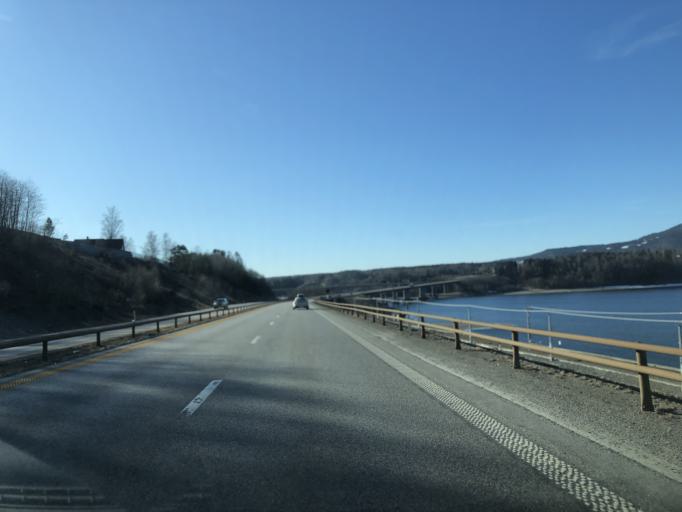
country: NO
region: Akershus
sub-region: Eidsvoll
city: Eidsvoll
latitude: 60.4063
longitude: 11.2375
